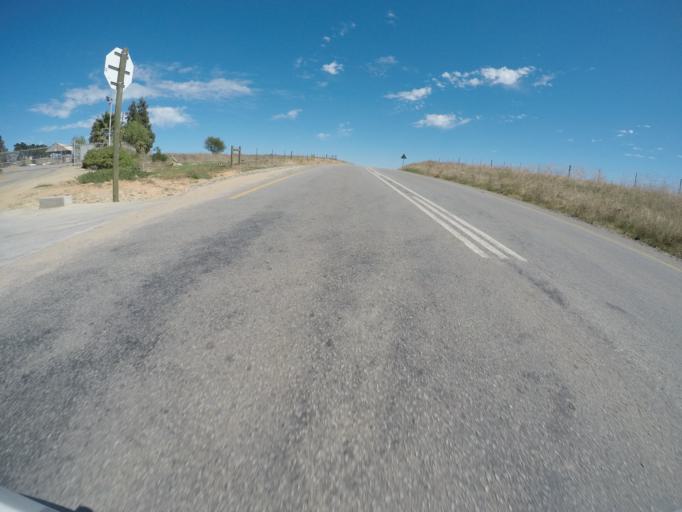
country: ZA
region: Western Cape
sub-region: West Coast District Municipality
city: Malmesbury
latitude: -33.4791
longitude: 18.7121
